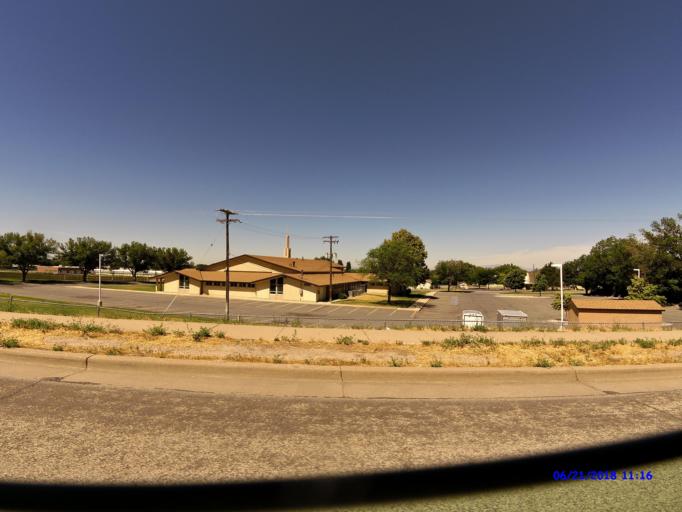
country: US
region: Utah
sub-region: Weber County
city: Ogden
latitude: 41.2583
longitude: -111.9560
